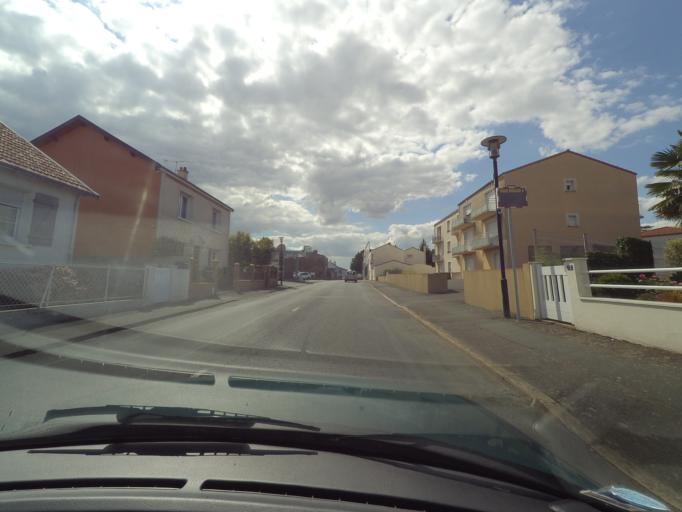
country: FR
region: Pays de la Loire
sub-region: Departement de la Vendee
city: Montaigu
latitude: 46.9782
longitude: -1.3075
